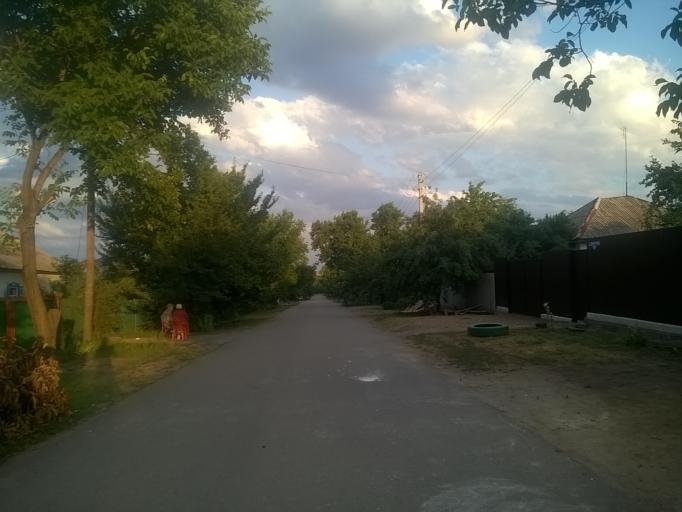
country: RU
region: Rostov
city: Donetsk
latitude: 48.3349
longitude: 39.9569
